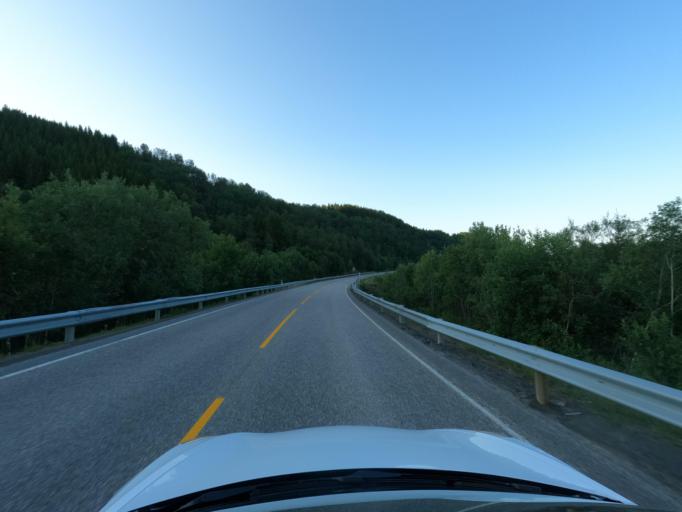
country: NO
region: Troms
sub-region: Harstad
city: Harstad
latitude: 68.7280
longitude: 16.5415
